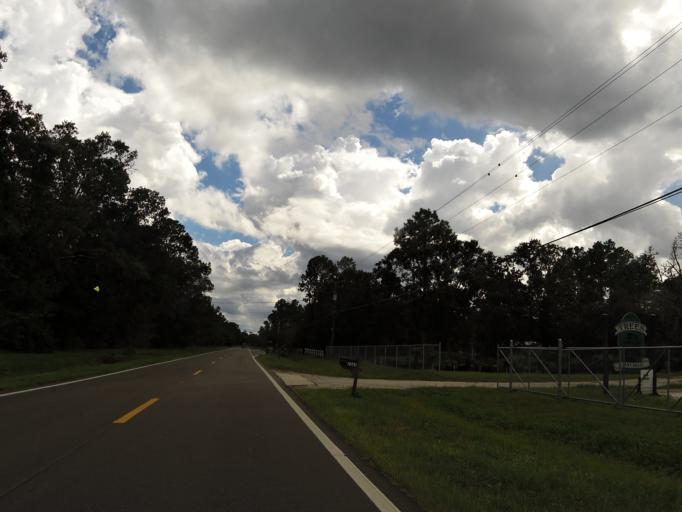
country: US
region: Florida
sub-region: Saint Johns County
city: Saint Augustine
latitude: 29.9199
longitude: -81.4959
